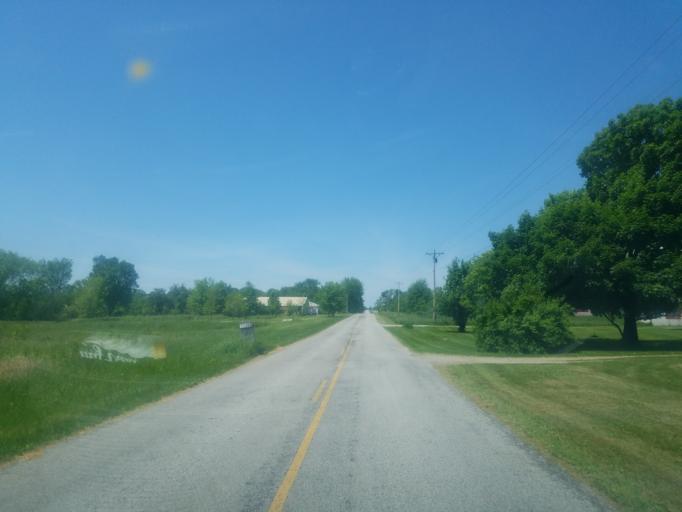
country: US
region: Ohio
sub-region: Huron County
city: New London
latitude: 41.1160
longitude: -82.3740
